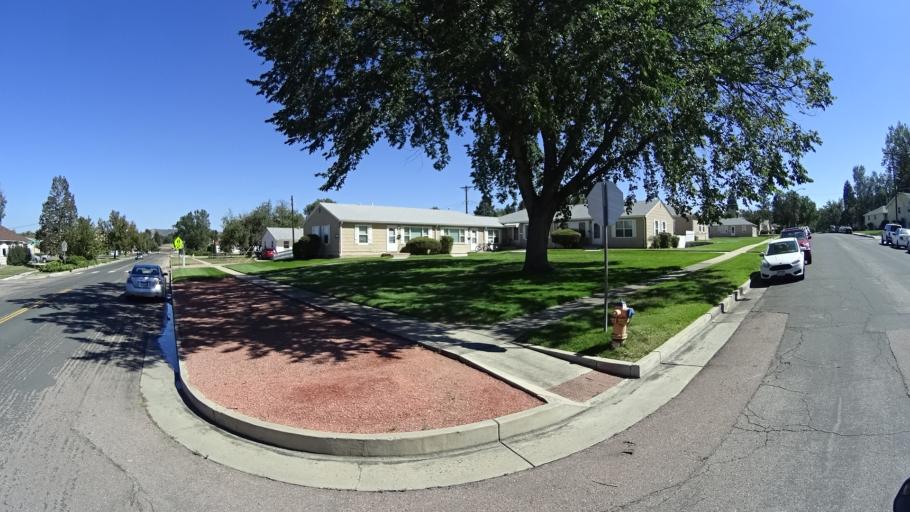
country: US
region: Colorado
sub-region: El Paso County
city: Colorado Springs
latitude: 38.8523
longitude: -104.8028
